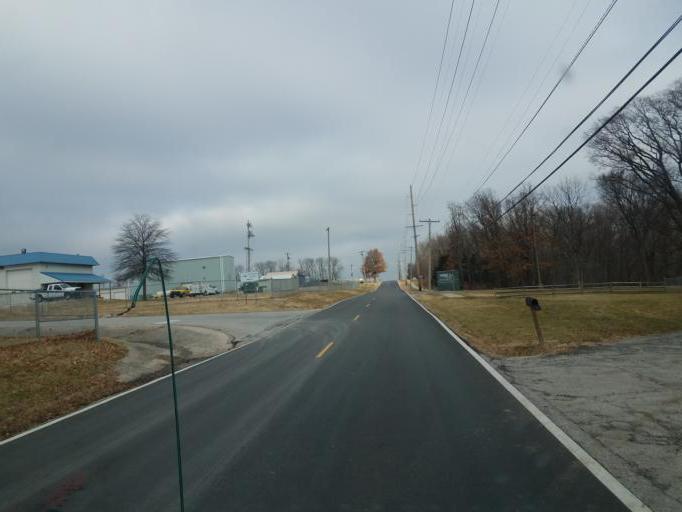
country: US
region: Missouri
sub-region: Greene County
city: Springfield
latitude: 37.2402
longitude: -93.2291
